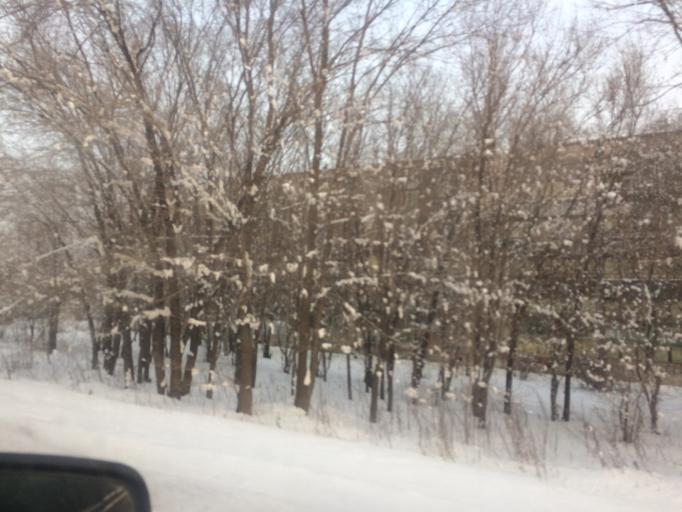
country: RU
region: Chelyabinsk
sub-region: Gorod Magnitogorsk
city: Magnitogorsk
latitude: 53.4700
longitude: 59.0758
